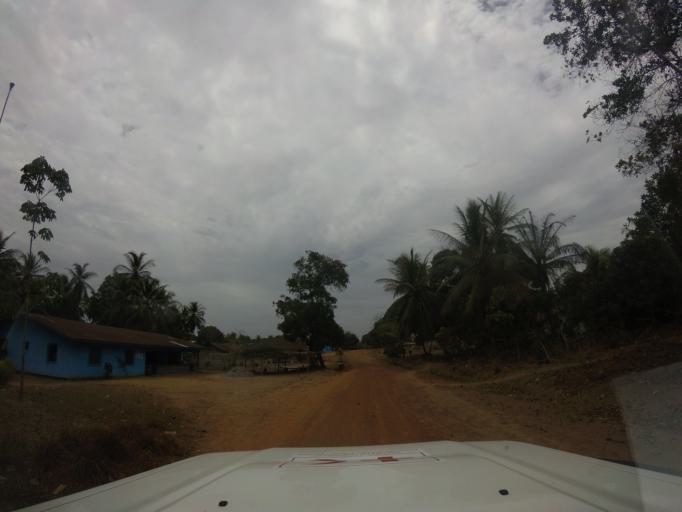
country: LR
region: Grand Cape Mount
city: Robertsport
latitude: 6.9355
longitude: -11.3313
